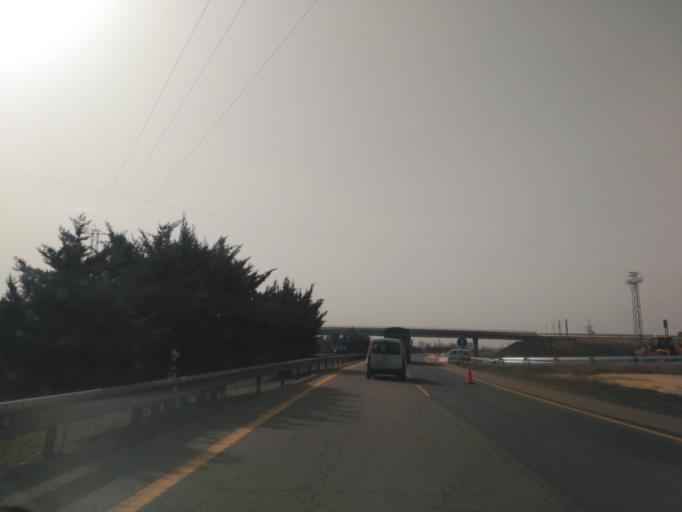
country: ES
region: Castille and Leon
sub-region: Provincia de Valladolid
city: Cabezon
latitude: 41.7573
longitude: -4.6344
